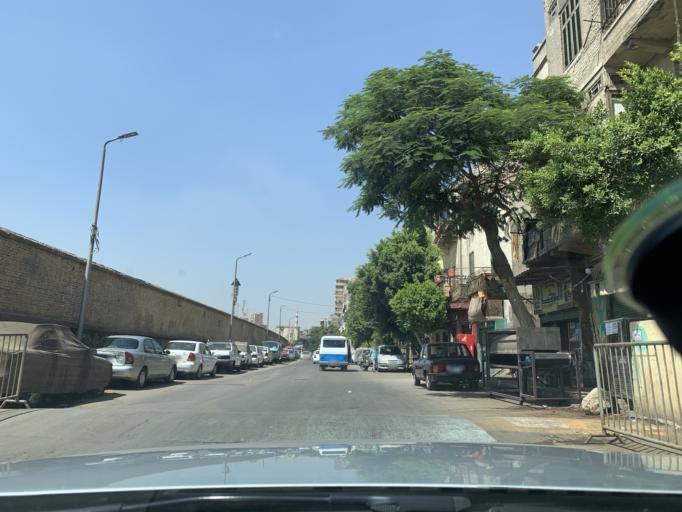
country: EG
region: Muhafazat al Qahirah
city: Cairo
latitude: 30.0681
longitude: 31.2540
